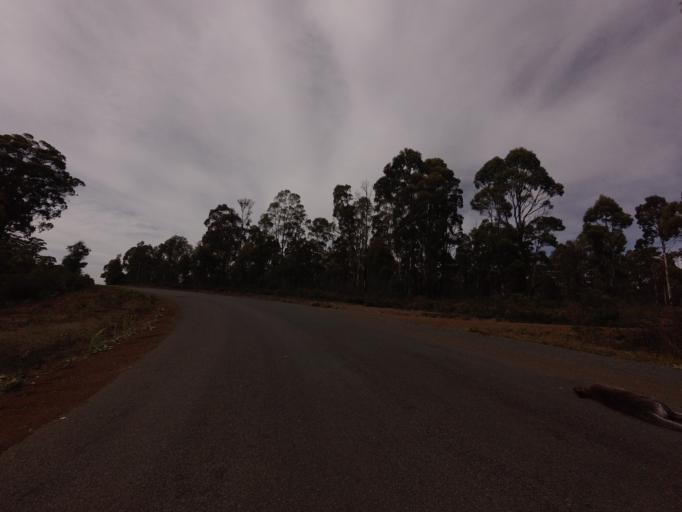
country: AU
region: Tasmania
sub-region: Sorell
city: Sorell
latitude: -42.5144
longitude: 147.6433
